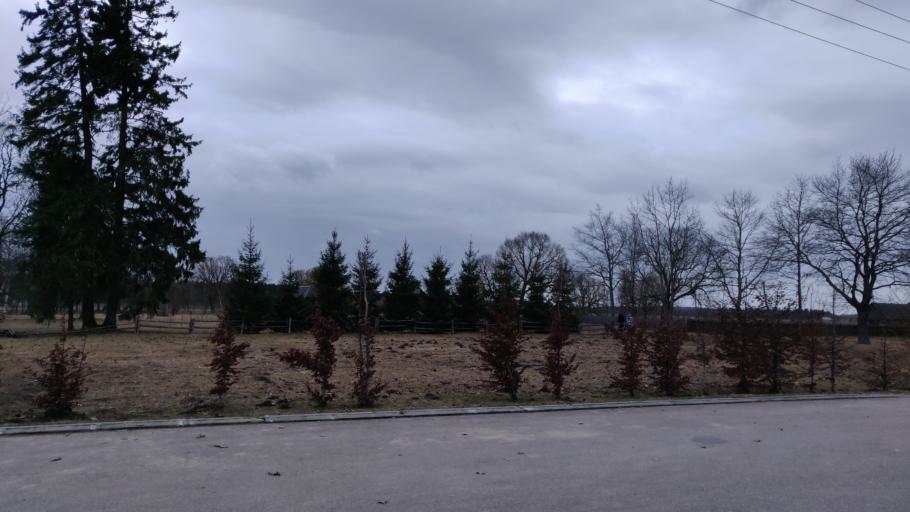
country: LT
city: Raseiniai
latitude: 55.4316
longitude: 23.3270
